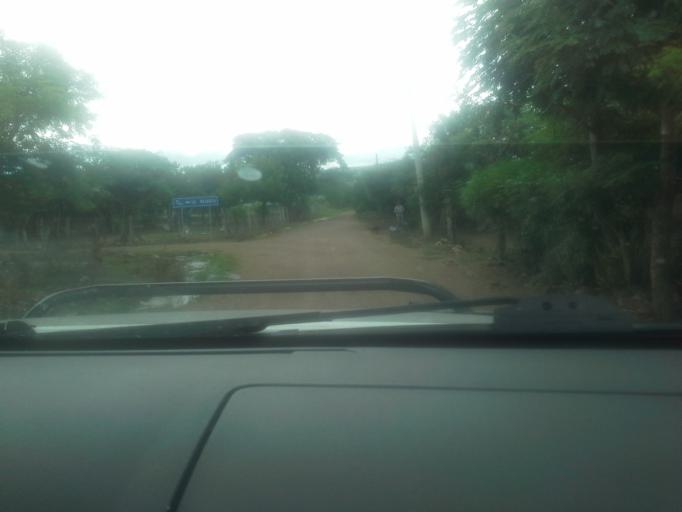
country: NI
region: Matagalpa
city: Ciudad Dario
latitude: 12.8147
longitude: -86.1930
